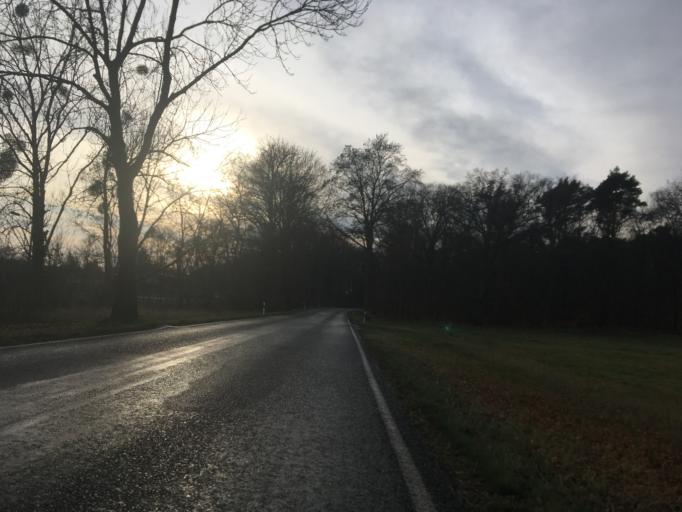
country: DE
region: Brandenburg
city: Eberswalde
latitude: 52.8499
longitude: 13.8473
